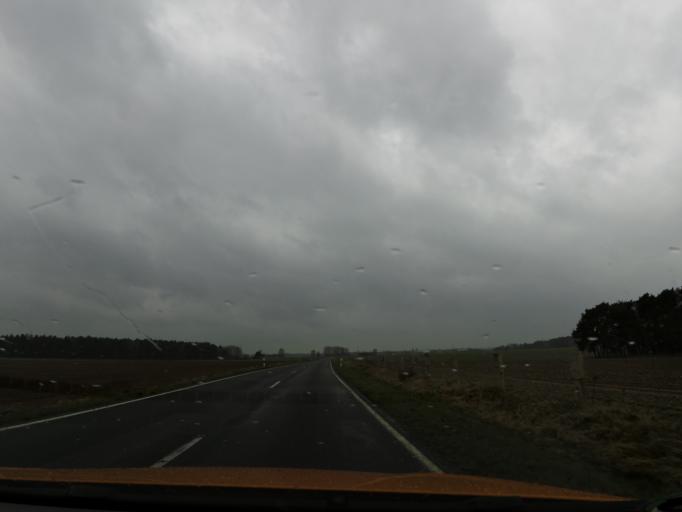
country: DE
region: Brandenburg
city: Ziesar
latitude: 52.2771
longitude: 12.3212
